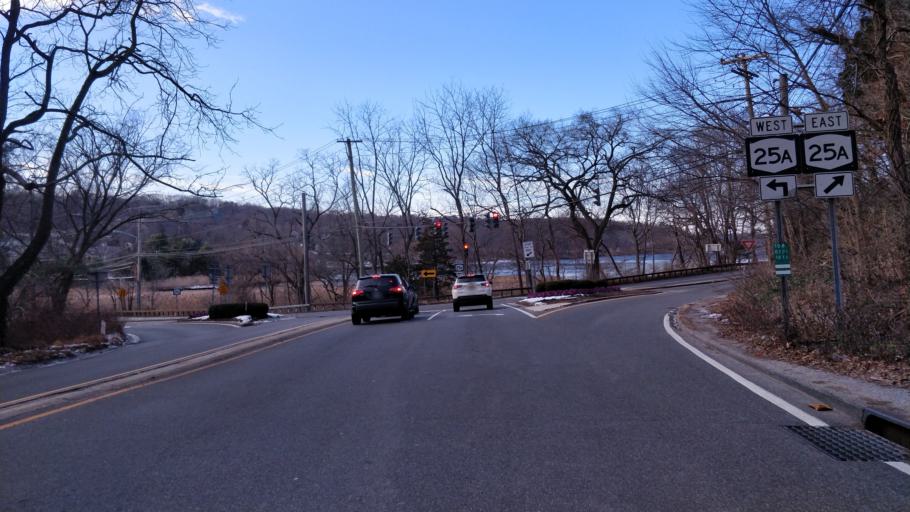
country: US
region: New York
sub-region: Nassau County
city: Laurel Hollow
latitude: 40.8582
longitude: -73.4613
